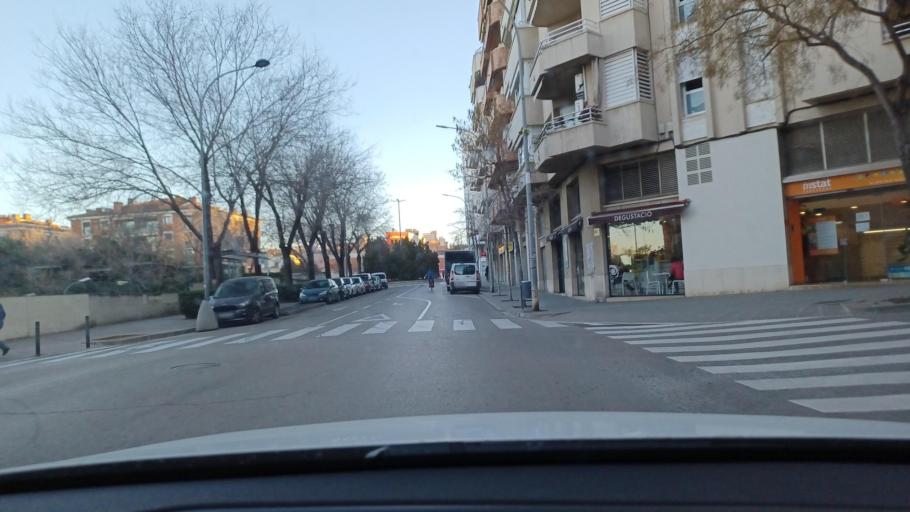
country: ES
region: Catalonia
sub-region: Provincia de Barcelona
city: Vilafranca del Penedes
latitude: 41.3452
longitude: 1.6934
